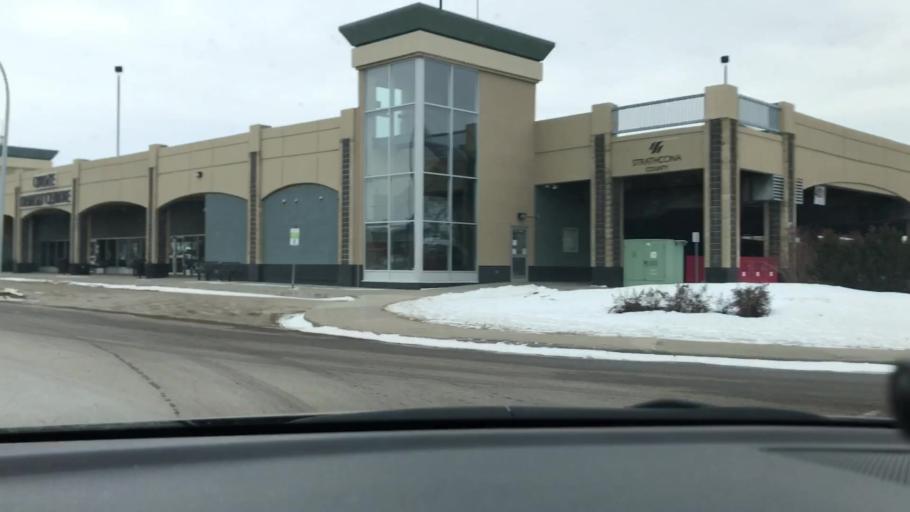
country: CA
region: Alberta
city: Sherwood Park
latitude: 53.5131
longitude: -113.3296
